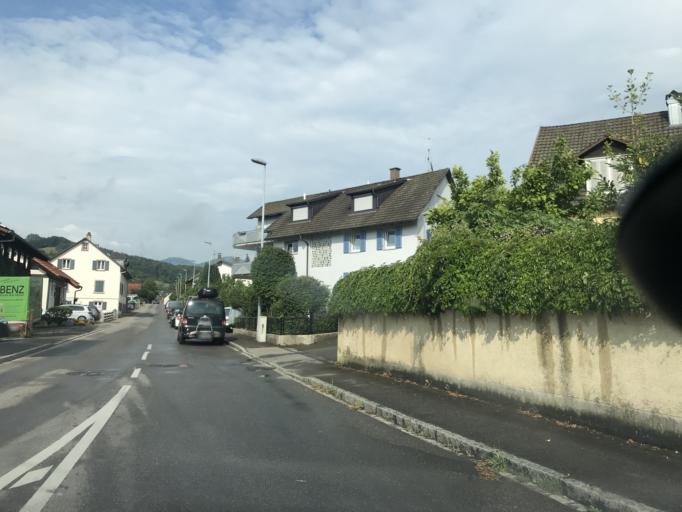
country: DE
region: Baden-Wuerttemberg
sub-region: Freiburg Region
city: Kandern
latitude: 47.7116
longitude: 7.6596
